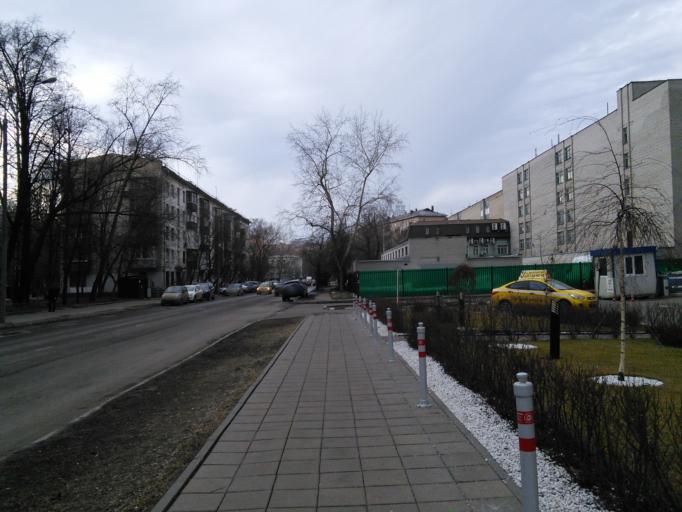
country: RU
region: Moscow
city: Sokol
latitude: 55.8058
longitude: 37.5447
